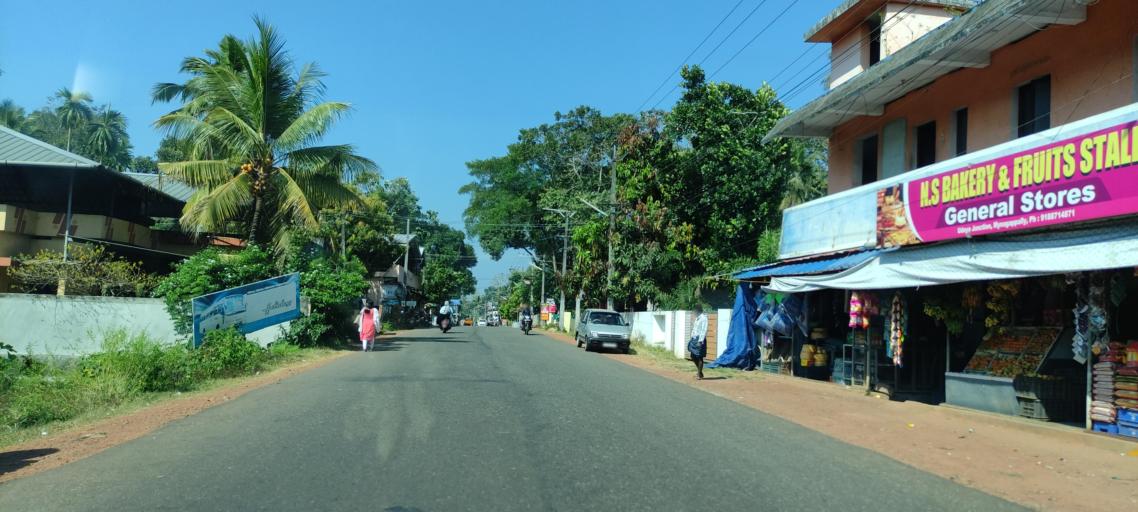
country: IN
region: Kerala
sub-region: Kollam
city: Panmana
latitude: 9.0415
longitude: 76.5915
